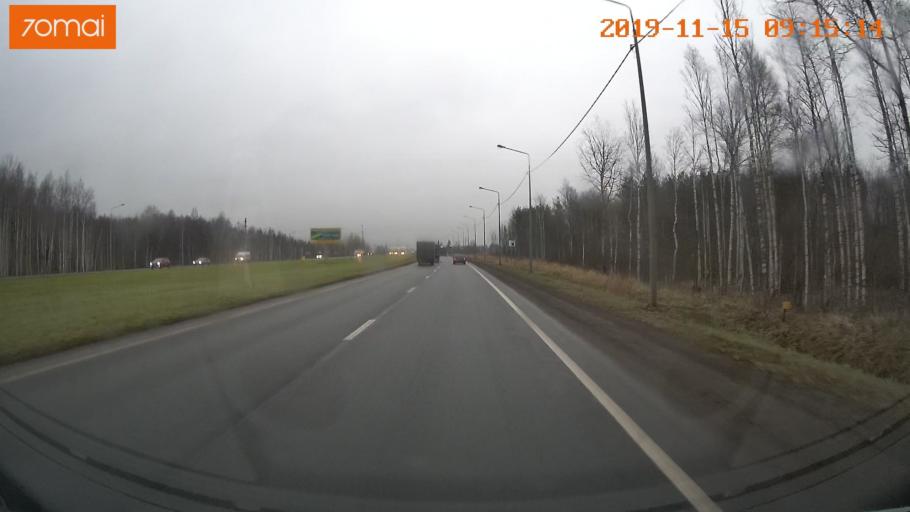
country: RU
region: Vologda
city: Tonshalovo
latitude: 59.2363
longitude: 37.9654
